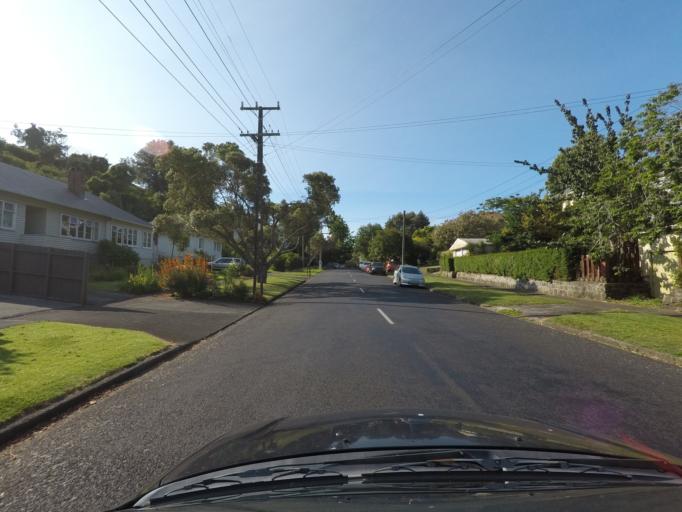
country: NZ
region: Auckland
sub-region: Auckland
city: Auckland
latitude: -36.9067
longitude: 174.7517
